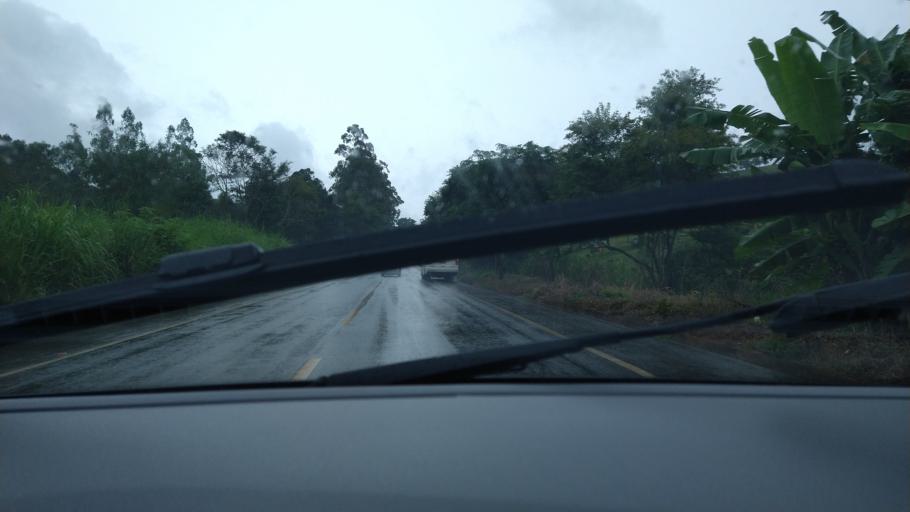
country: BR
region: Minas Gerais
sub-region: Vicosa
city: Vicosa
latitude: -20.6220
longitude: -42.8688
